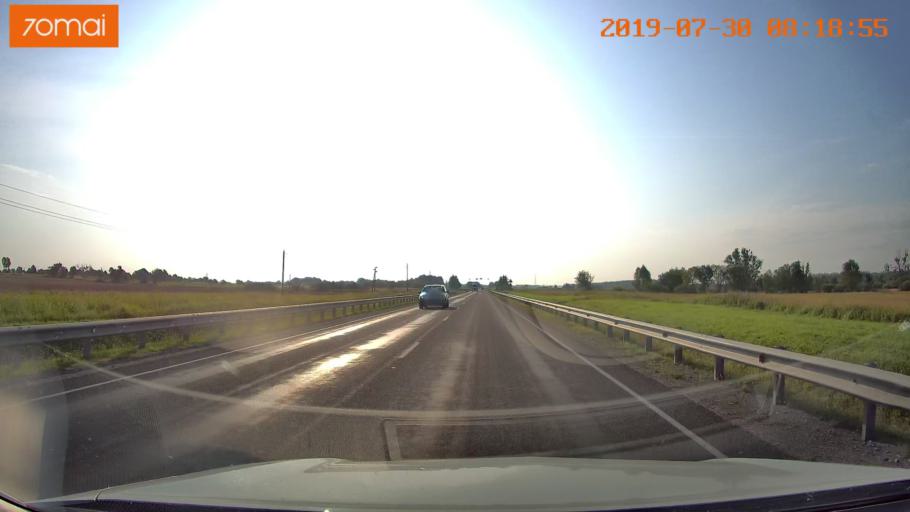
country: RU
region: Kaliningrad
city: Zheleznodorozhnyy
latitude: 54.6305
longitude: 21.4772
